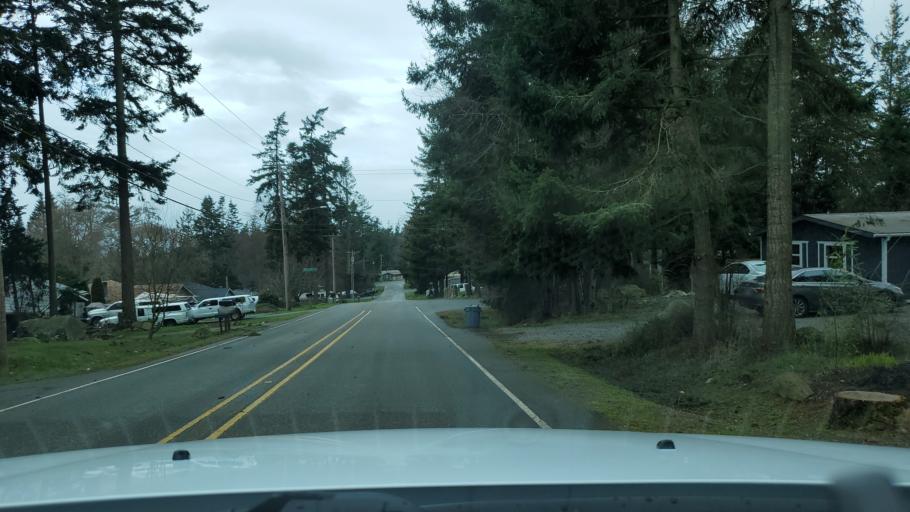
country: US
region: Washington
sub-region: Island County
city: Ault Field
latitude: 48.3661
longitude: -122.6458
